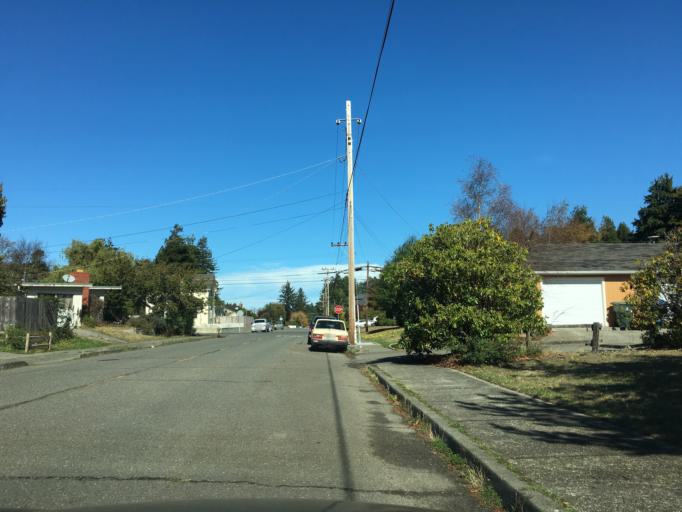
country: US
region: California
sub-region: Humboldt County
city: Cutten
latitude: 40.7798
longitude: -124.1481
